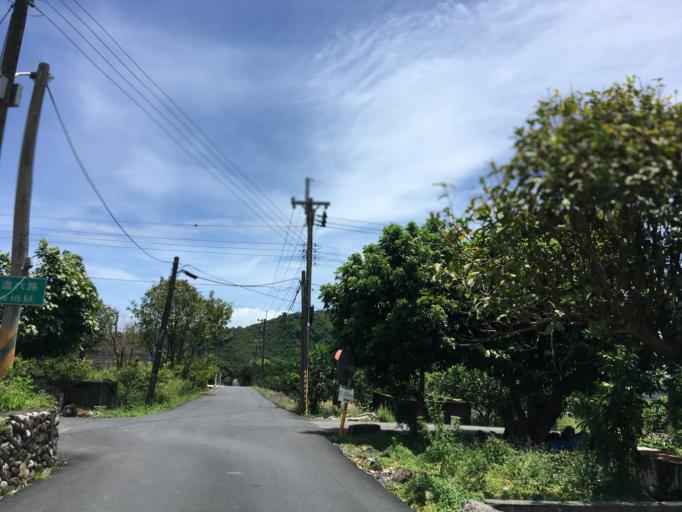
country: TW
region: Taiwan
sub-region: Yilan
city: Yilan
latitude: 24.6339
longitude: 121.7168
